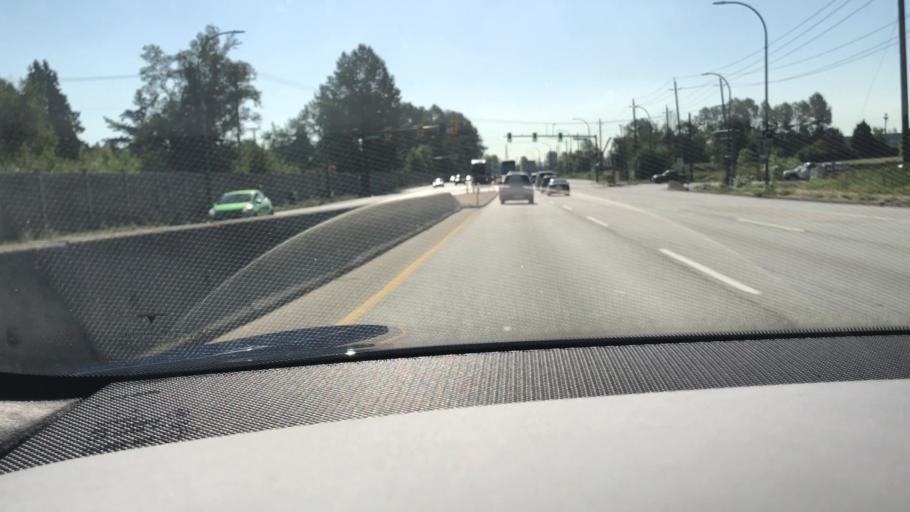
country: CA
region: British Columbia
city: New Westminster
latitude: 49.1968
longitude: -122.9700
